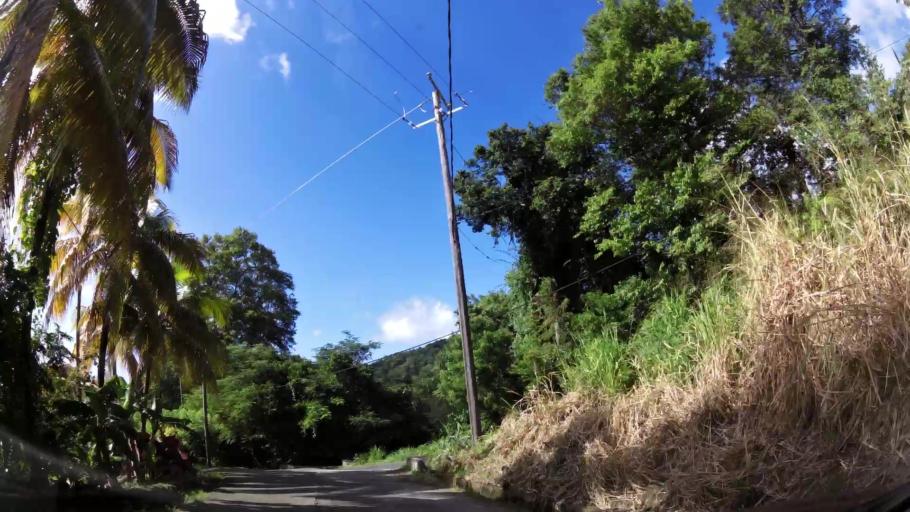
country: DM
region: Saint George
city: Roseau
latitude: 15.2849
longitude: -61.3694
